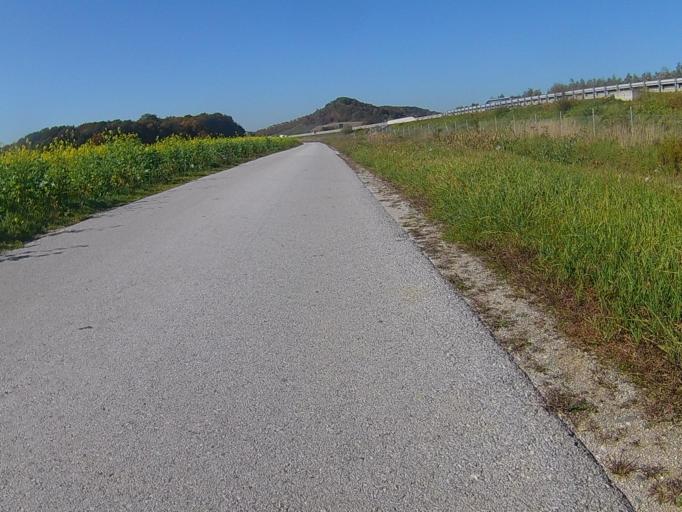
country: SI
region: Pesnica
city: Pesnica pri Mariboru
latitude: 46.5902
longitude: 15.7130
